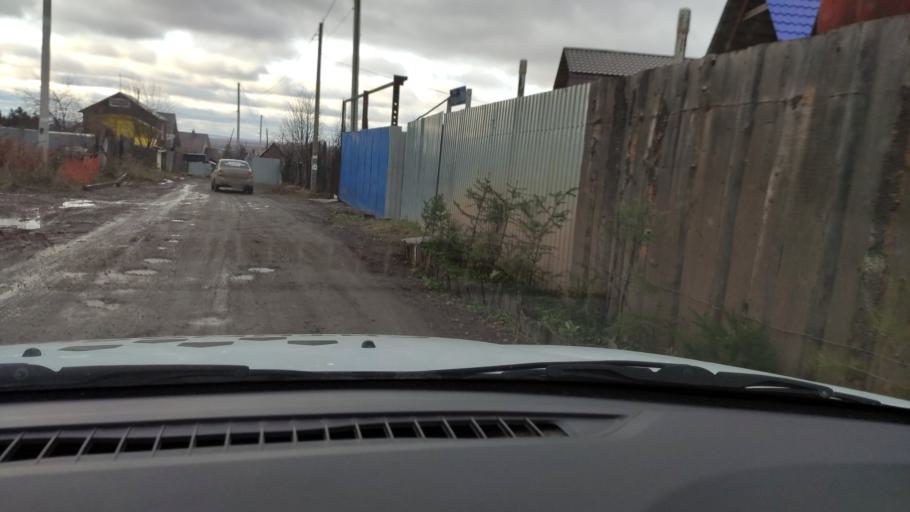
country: RU
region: Perm
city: Kondratovo
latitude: 57.9553
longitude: 56.1607
